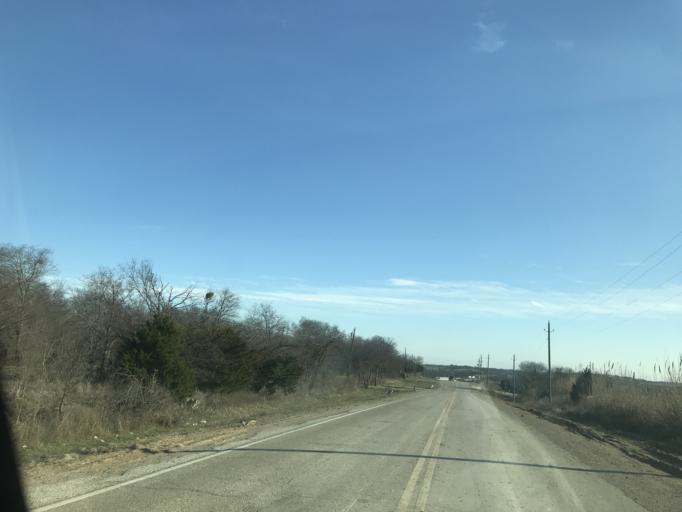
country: US
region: Texas
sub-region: Dallas County
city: Wilmer
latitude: 32.5658
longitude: -96.6690
